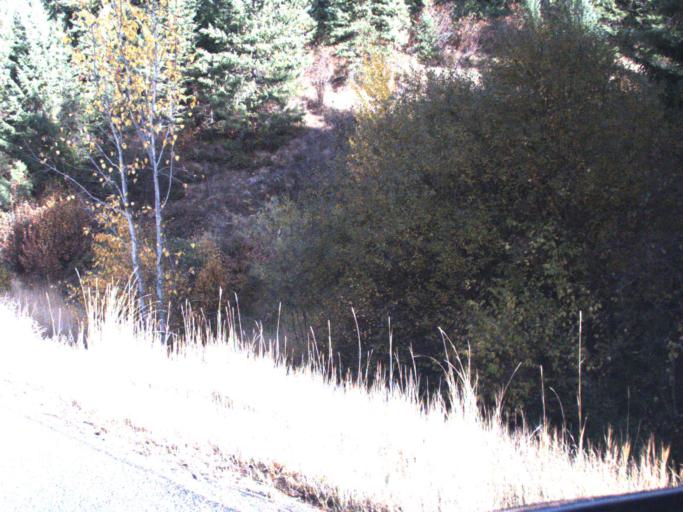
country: US
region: Washington
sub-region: Stevens County
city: Kettle Falls
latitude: 48.6768
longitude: -118.0201
